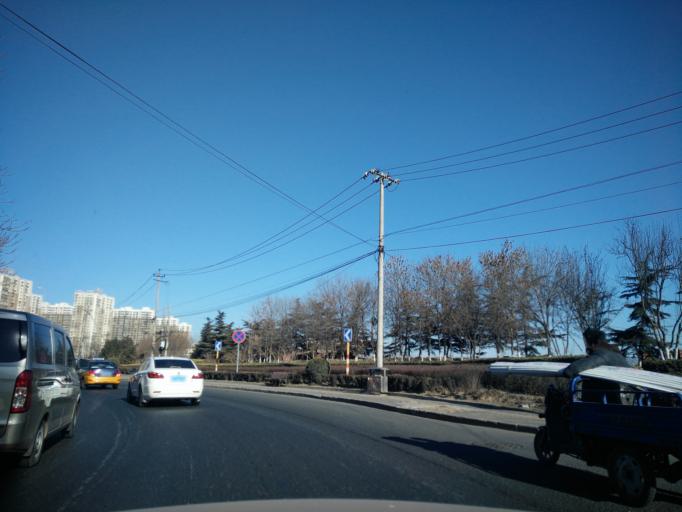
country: CN
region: Beijing
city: Xihongmen
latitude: 39.7781
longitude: 116.3391
